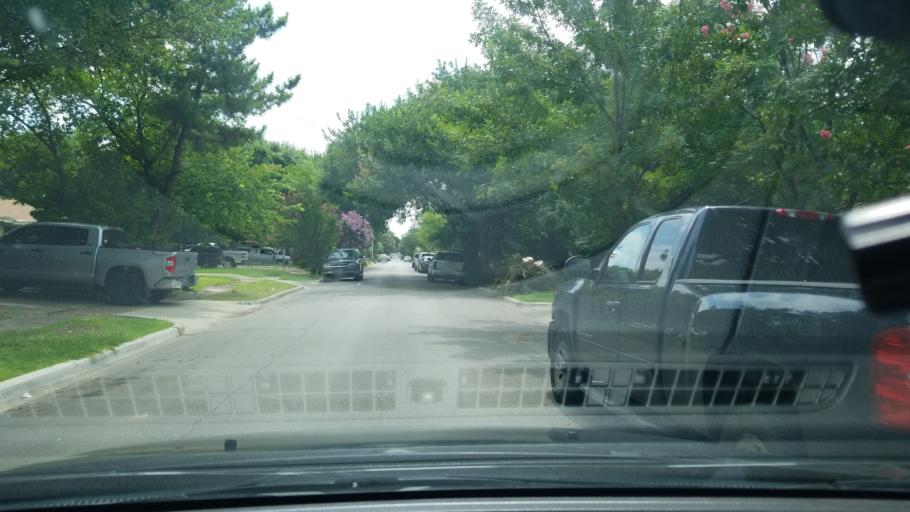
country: US
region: Texas
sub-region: Dallas County
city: Mesquite
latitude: 32.8133
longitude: -96.6719
